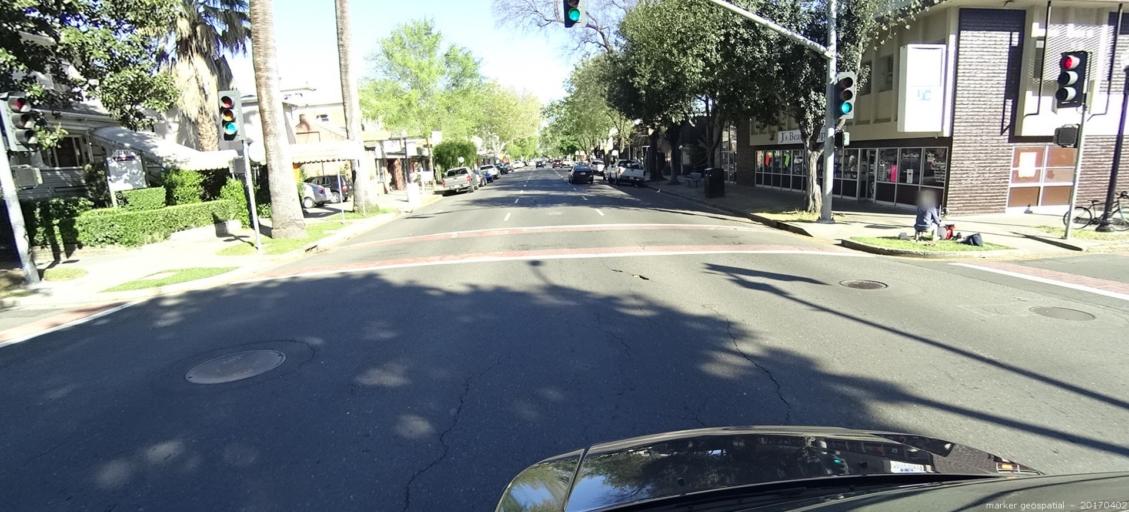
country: US
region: California
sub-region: Sacramento County
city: Sacramento
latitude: 38.5757
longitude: -121.4761
